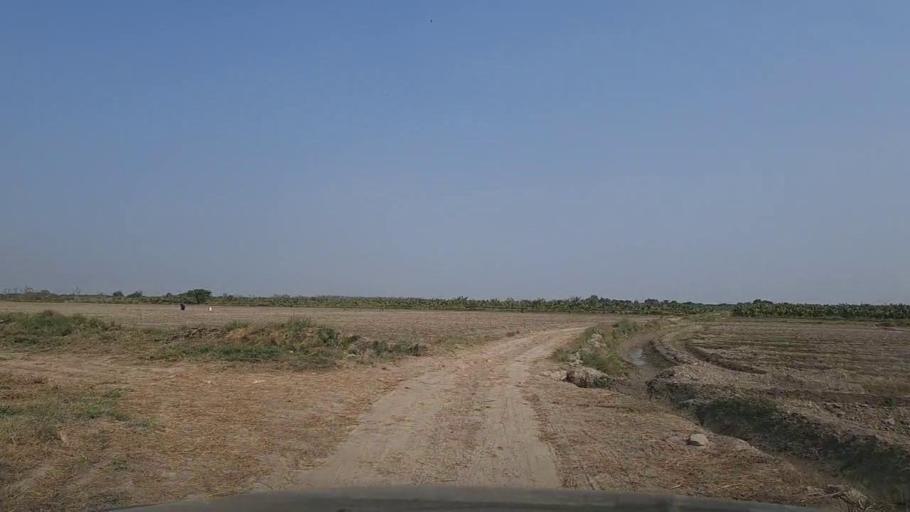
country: PK
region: Sindh
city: Thatta
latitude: 24.5693
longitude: 67.9197
